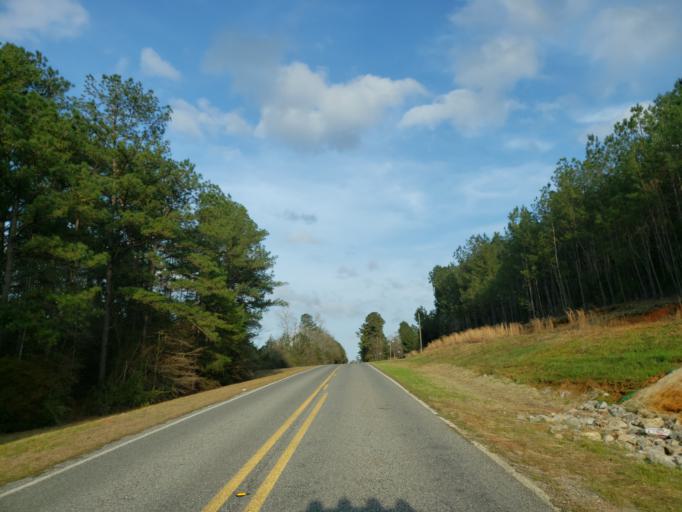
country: US
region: Mississippi
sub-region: Clarke County
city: Stonewall
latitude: 32.1719
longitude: -88.6929
